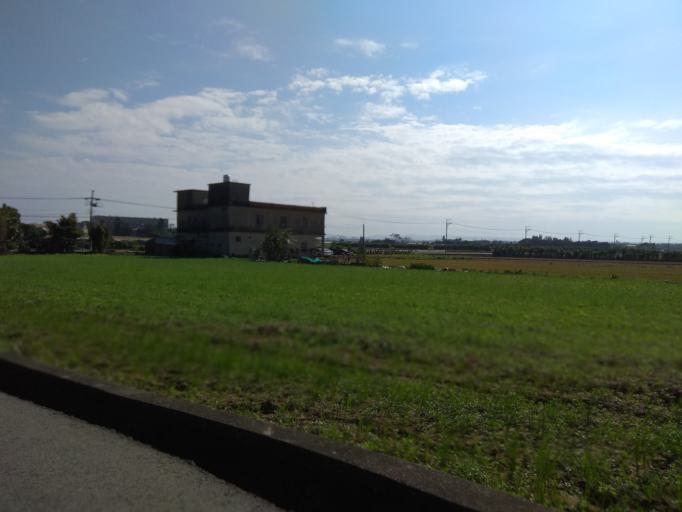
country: TW
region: Taiwan
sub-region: Hsinchu
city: Zhubei
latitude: 24.9500
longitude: 121.0136
